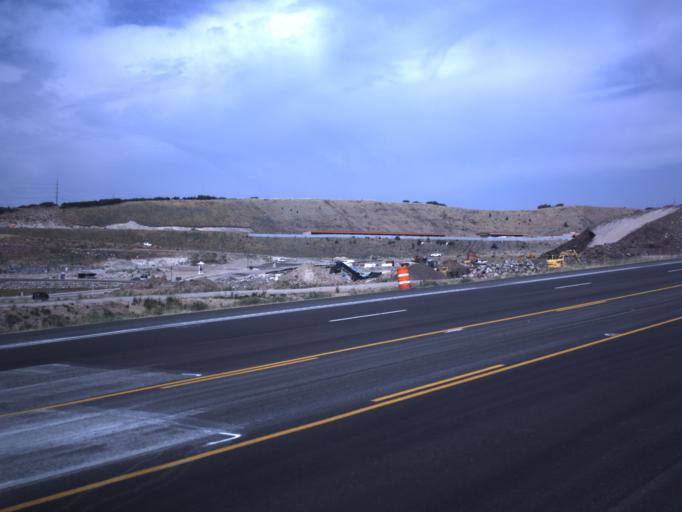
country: US
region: Utah
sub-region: Summit County
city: Park City
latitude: 40.6739
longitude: -111.4288
